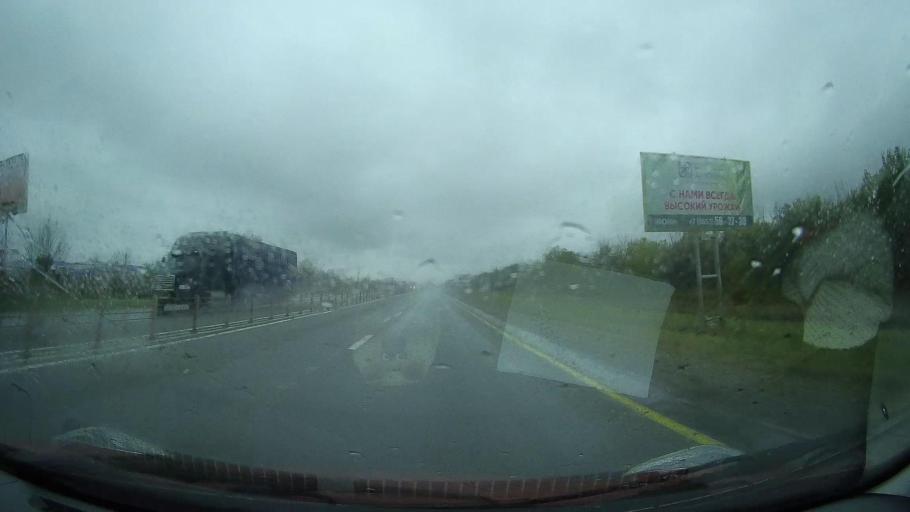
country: RU
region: Stavropol'skiy
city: Nevinnomyssk
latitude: 44.6400
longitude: 41.9726
